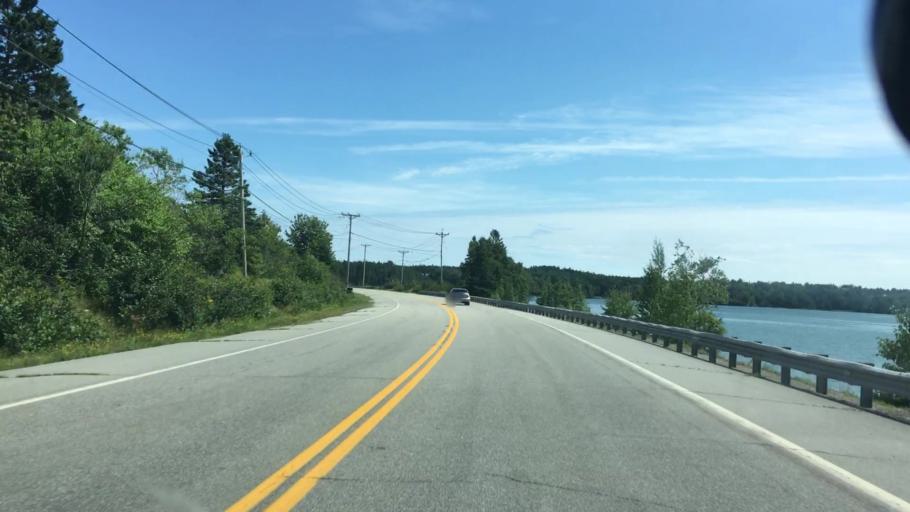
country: US
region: Maine
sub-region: Washington County
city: Eastport
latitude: 44.9405
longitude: -67.0366
